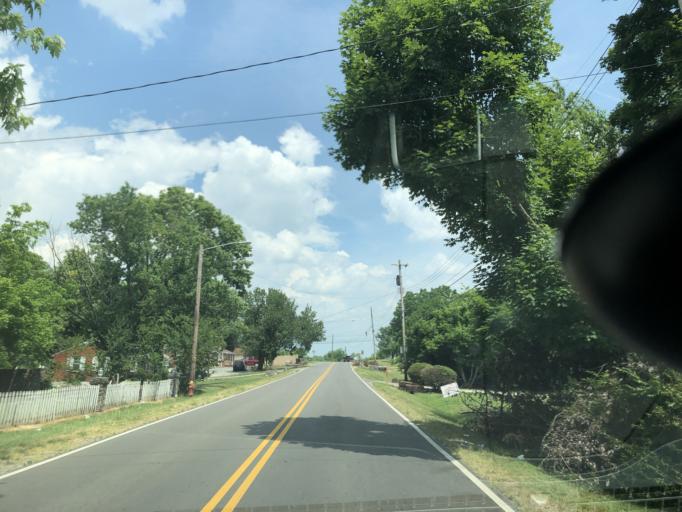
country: US
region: Tennessee
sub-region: Davidson County
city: Oak Hill
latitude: 36.0710
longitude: -86.6957
